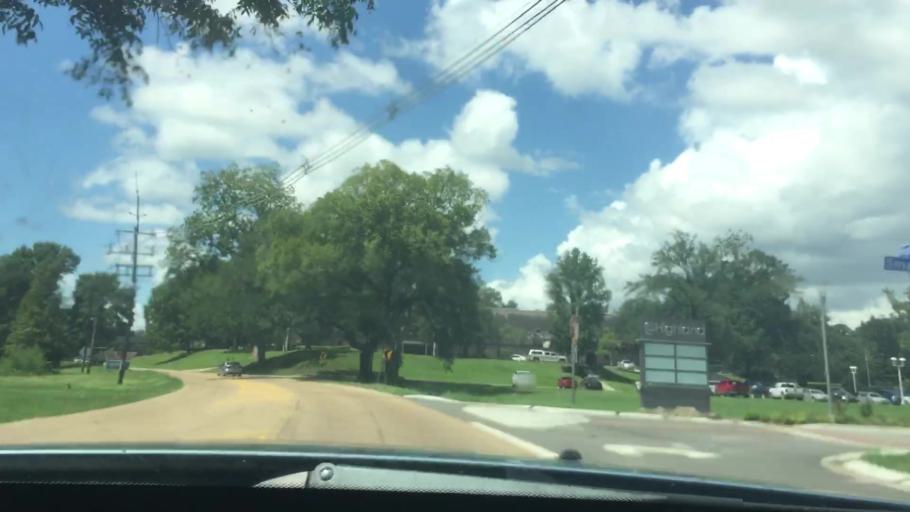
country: US
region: Louisiana
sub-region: East Baton Rouge Parish
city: Oak Hills Place
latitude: 30.3609
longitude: -91.1070
